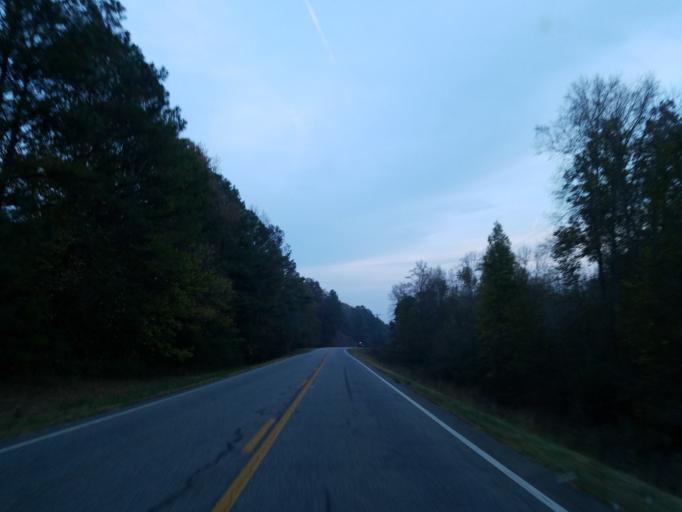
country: US
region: Georgia
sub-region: Gilmer County
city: Ellijay
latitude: 34.5699
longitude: -84.6119
